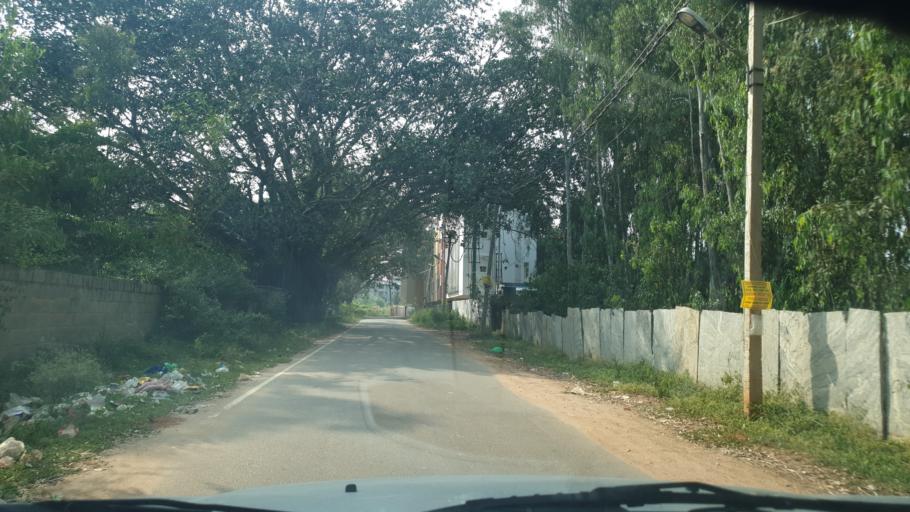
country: IN
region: Karnataka
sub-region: Bangalore Urban
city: Yelahanka
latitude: 13.0672
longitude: 77.6628
